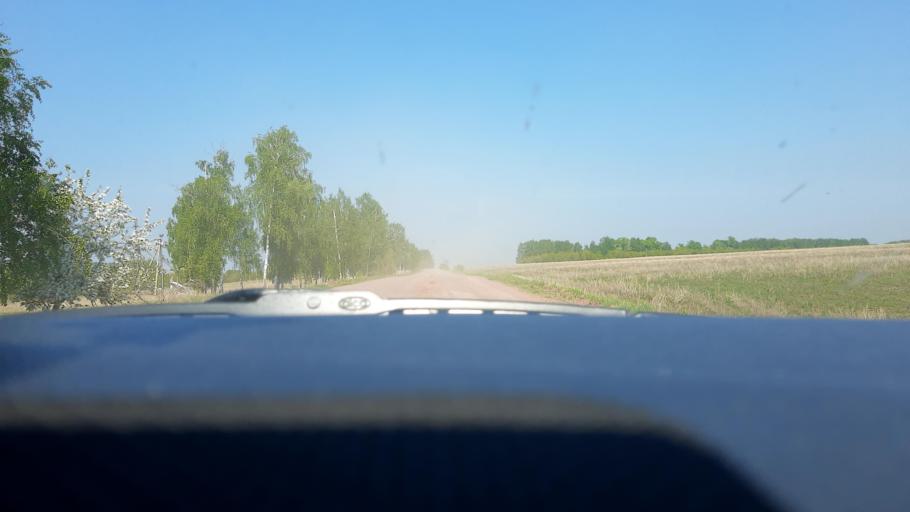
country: RU
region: Bashkortostan
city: Chishmy
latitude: 54.4326
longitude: 55.2960
